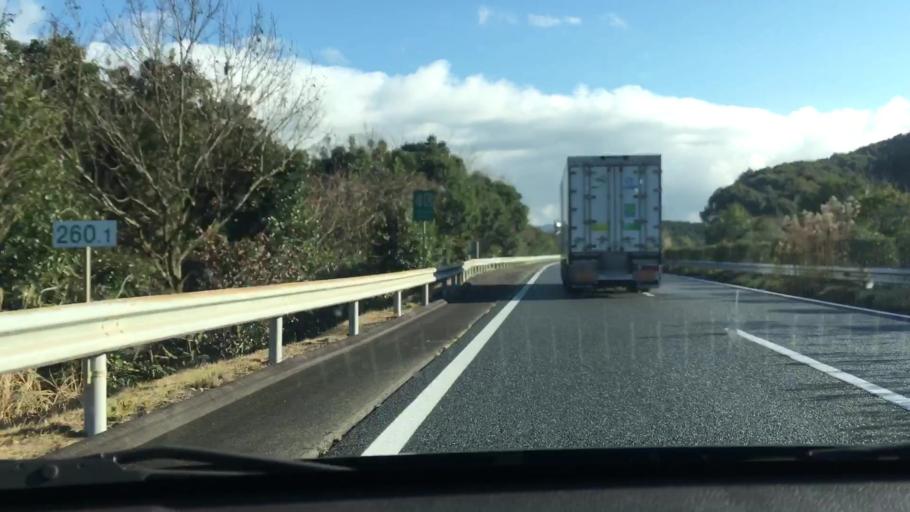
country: JP
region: Kumamoto
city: Hitoyoshi
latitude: 32.1707
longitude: 130.7916
